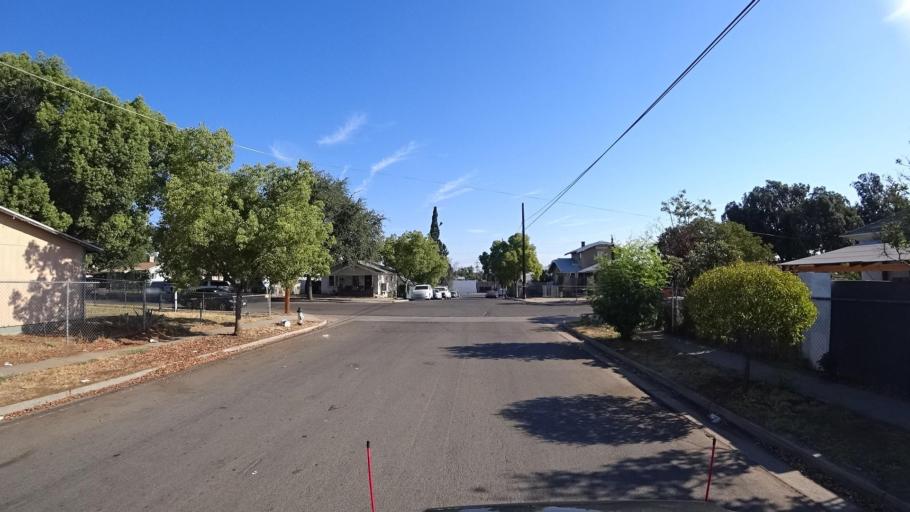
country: US
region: California
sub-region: Fresno County
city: Fresno
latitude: 36.7493
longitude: -119.7709
